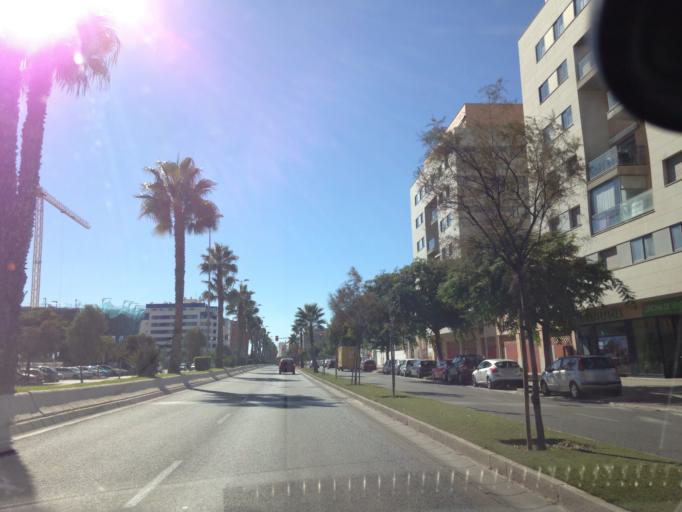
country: ES
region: Andalusia
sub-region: Provincia de Malaga
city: Malaga
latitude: 36.6985
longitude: -4.4374
